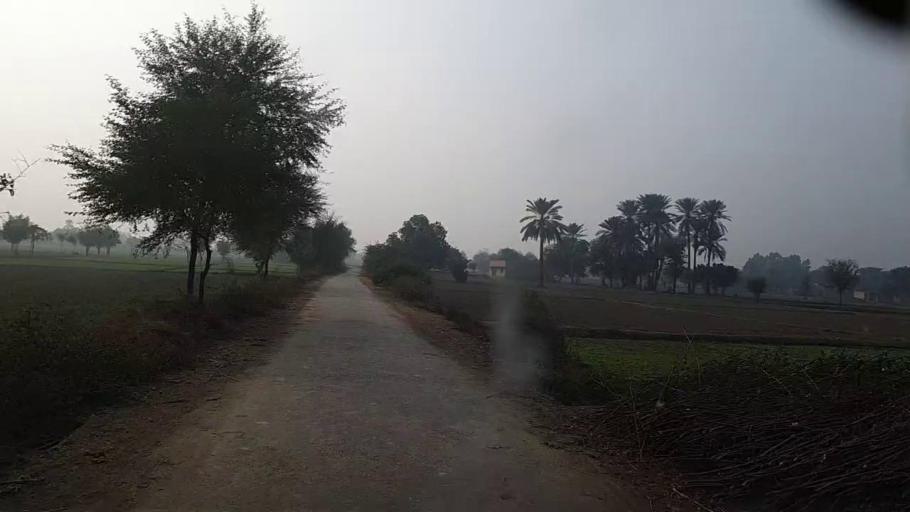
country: PK
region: Sindh
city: Bozdar
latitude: 27.1518
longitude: 68.6667
